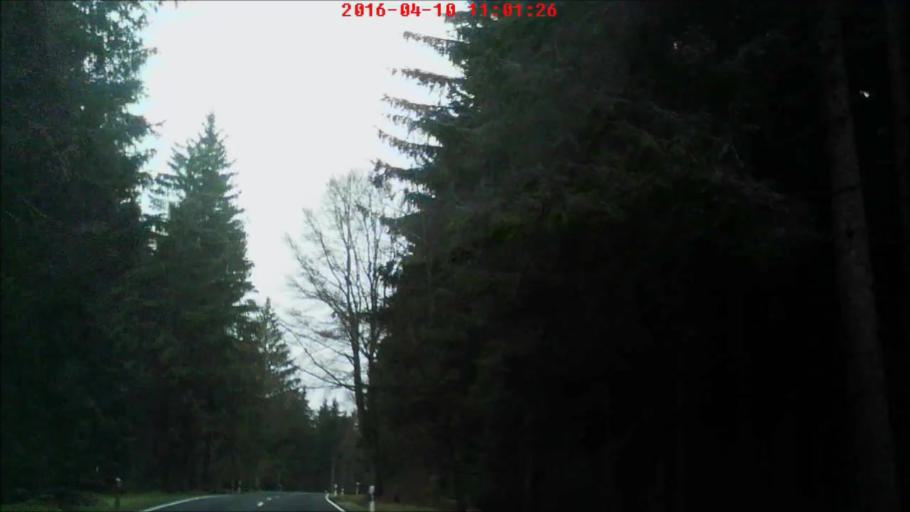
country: DE
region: Thuringia
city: Schmiedefeld am Rennsteig
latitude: 50.6042
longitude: 10.8485
